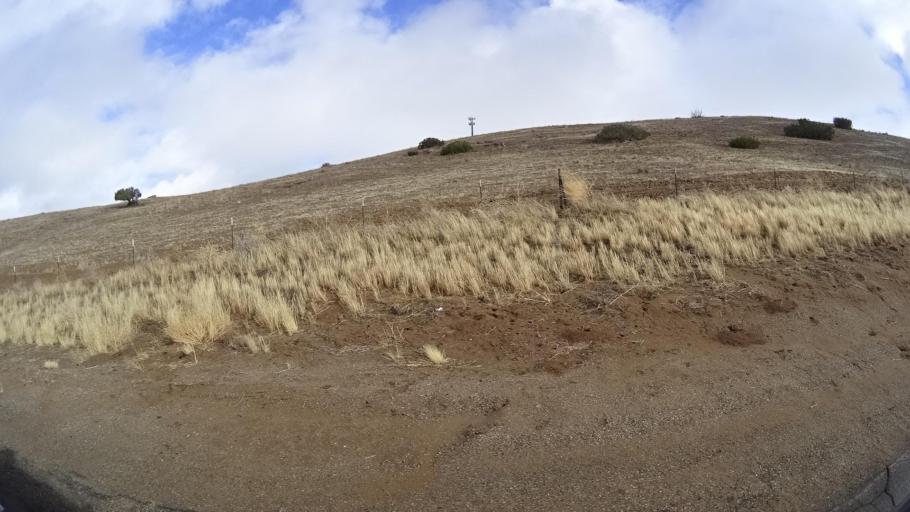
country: US
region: California
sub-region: Kern County
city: Maricopa
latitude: 34.9175
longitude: -119.4082
